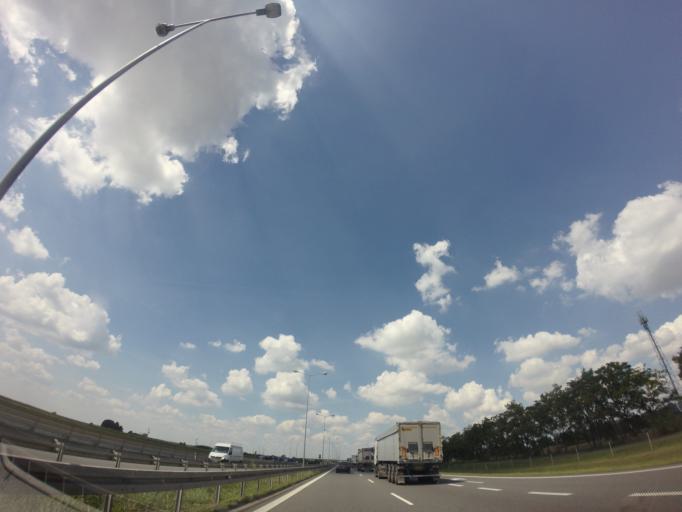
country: PL
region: Opole Voivodeship
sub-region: Powiat opolski
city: Proszkow
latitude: 50.5673
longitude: 17.8640
